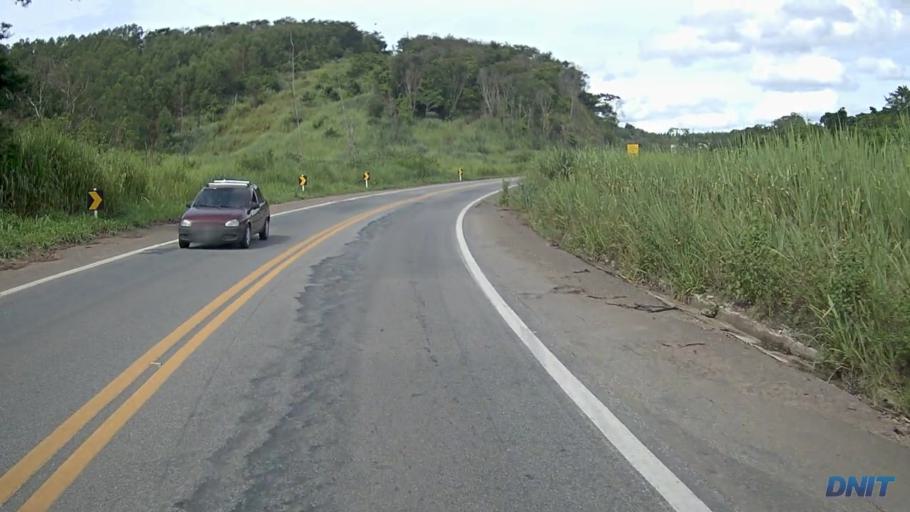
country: BR
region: Minas Gerais
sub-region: Ipaba
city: Ipaba
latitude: -19.3605
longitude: -42.4468
